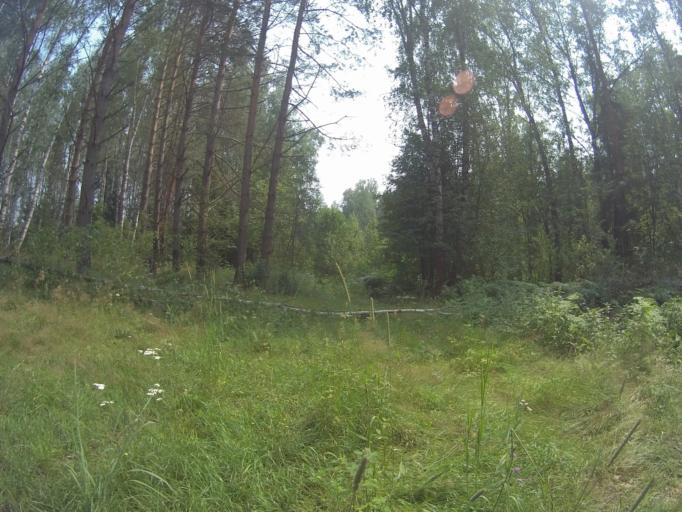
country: RU
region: Vladimir
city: Vorsha
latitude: 55.9805
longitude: 40.1944
